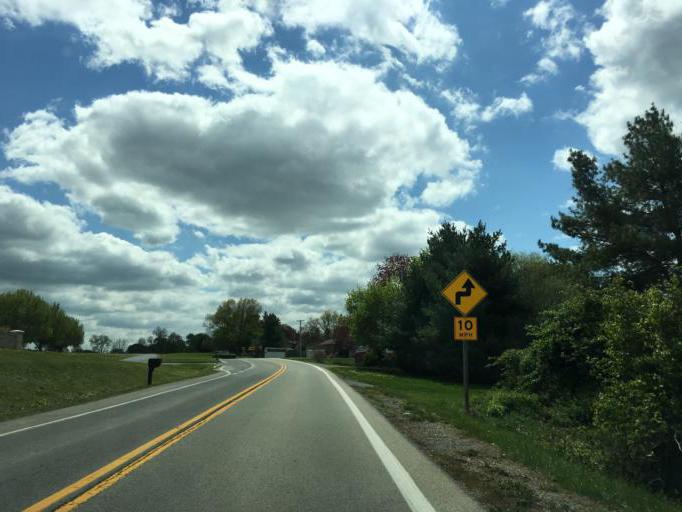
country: US
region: Maryland
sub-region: Frederick County
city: Thurmont
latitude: 39.6382
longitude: -77.4031
